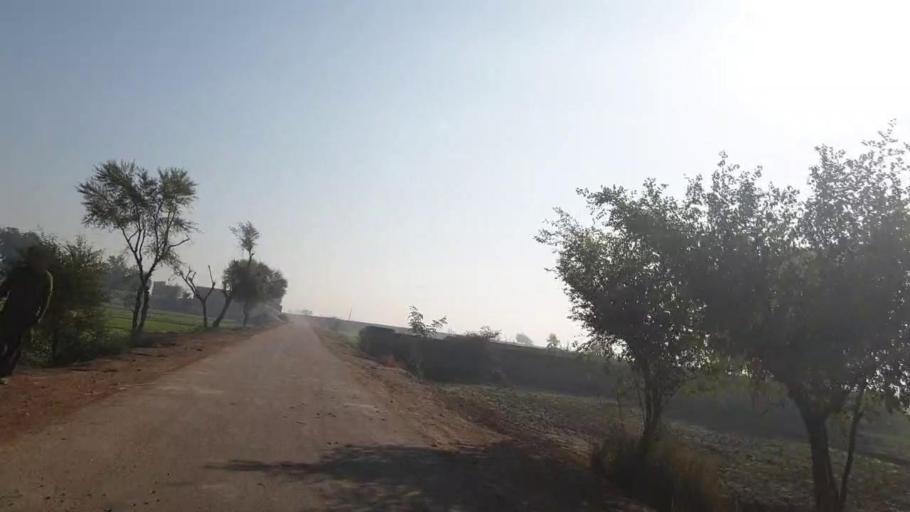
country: PK
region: Sindh
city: Dadu
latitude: 26.6736
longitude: 67.8110
